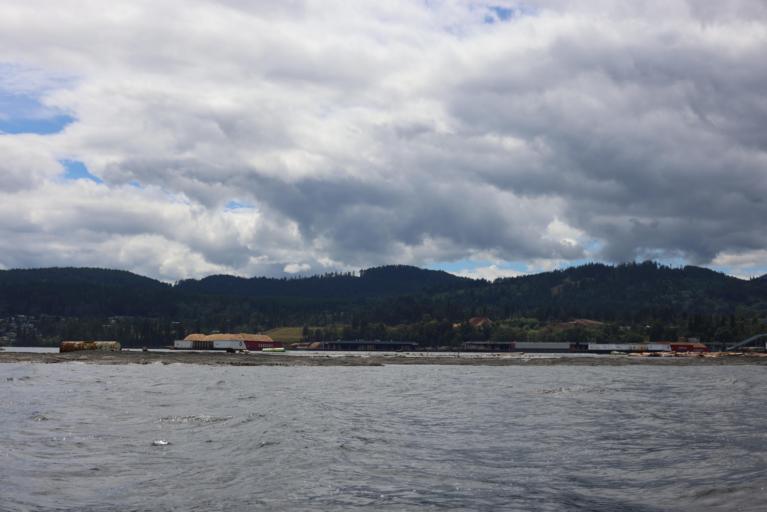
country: CA
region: British Columbia
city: North Cowichan
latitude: 48.8797
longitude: -123.6277
